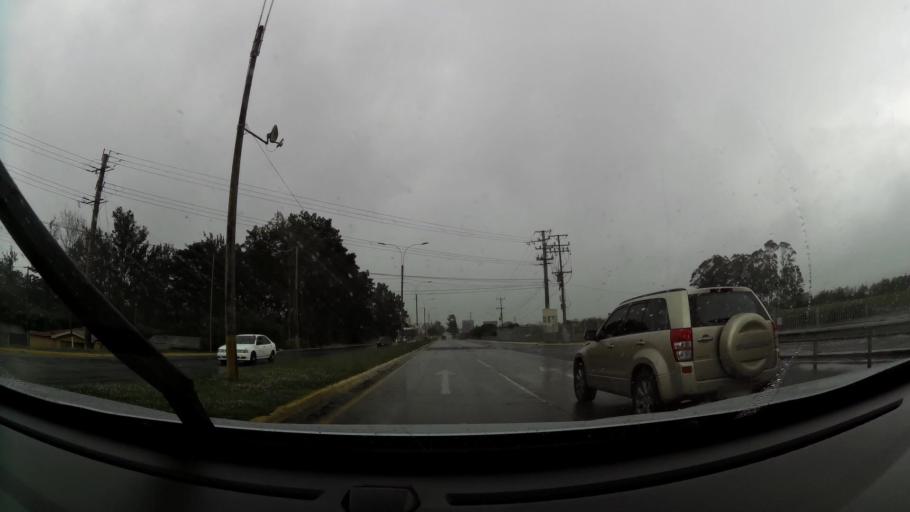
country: CR
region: Cartago
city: Cartago
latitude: 9.8678
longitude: -83.9412
